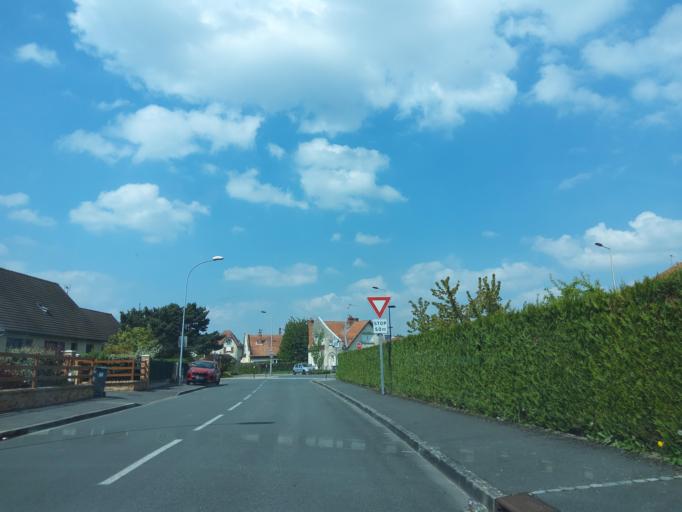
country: FR
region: Picardie
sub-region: Departement de l'Aisne
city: Laon
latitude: 49.5754
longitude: 3.6332
